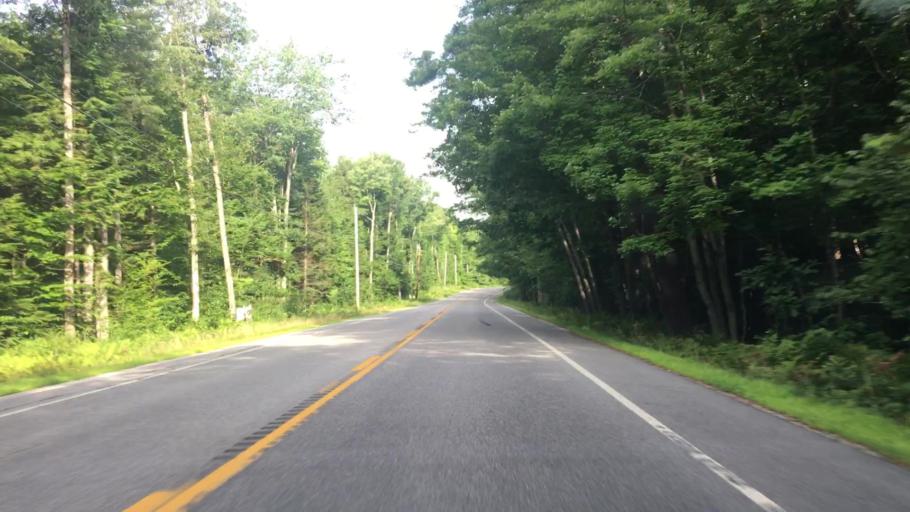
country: US
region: Maine
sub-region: York County
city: Limington
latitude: 43.7590
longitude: -70.7041
